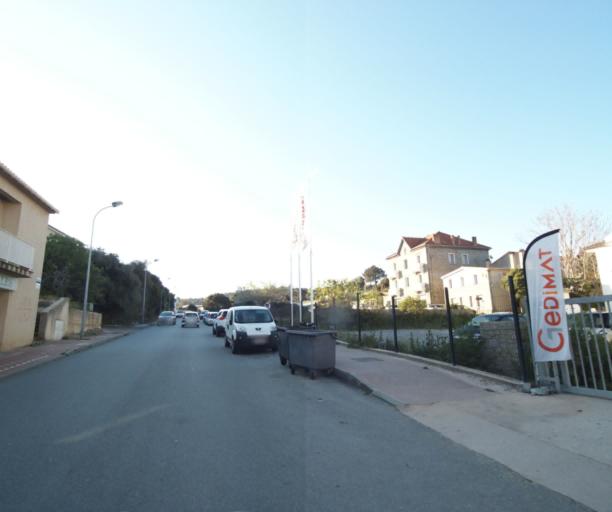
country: FR
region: Corsica
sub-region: Departement de la Corse-du-Sud
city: Propriano
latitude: 41.6738
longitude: 8.9063
